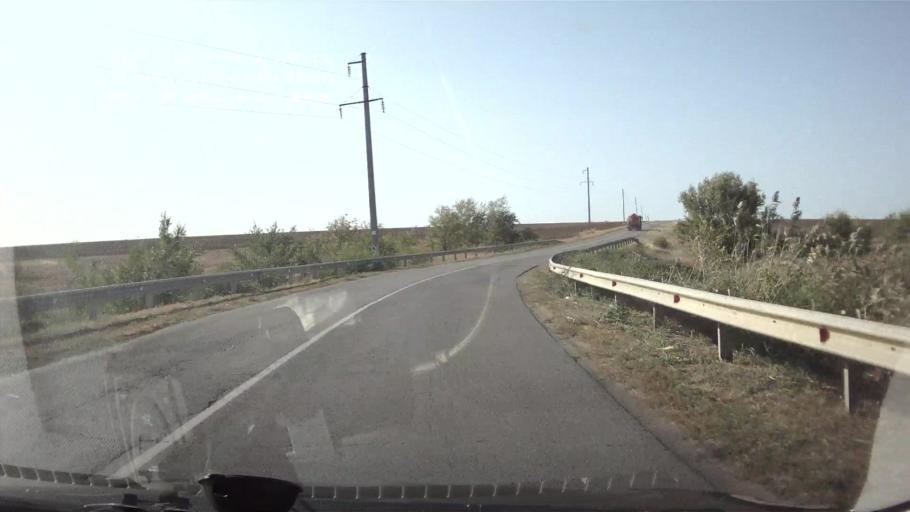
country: RU
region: Rostov
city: Tselina
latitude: 46.4709
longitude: 40.8788
